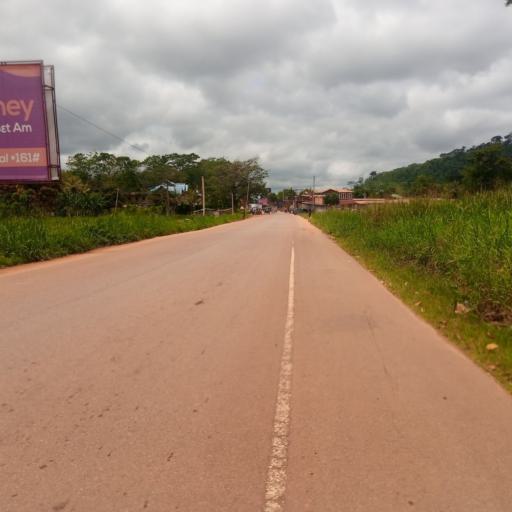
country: SL
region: Eastern Province
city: Kenema
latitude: 7.8525
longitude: -11.2052
